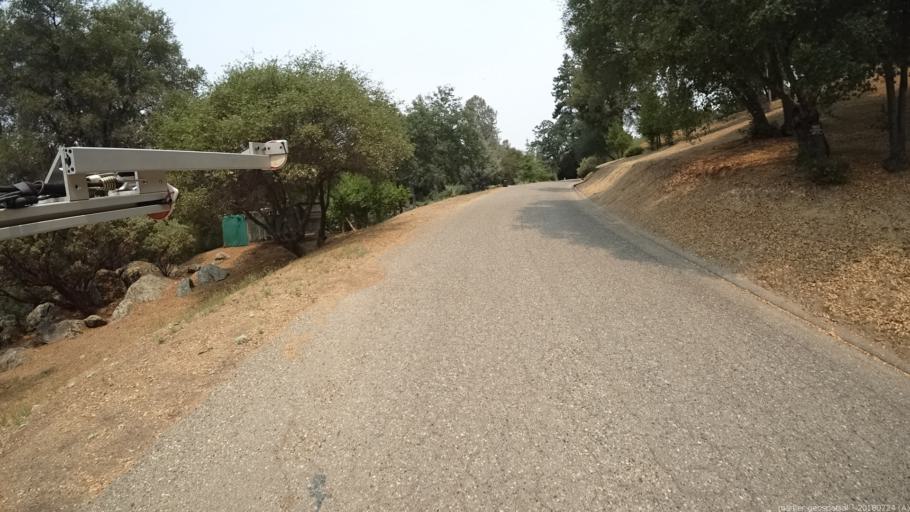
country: US
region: California
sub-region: Madera County
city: Oakhurst
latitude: 37.3177
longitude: -119.5997
